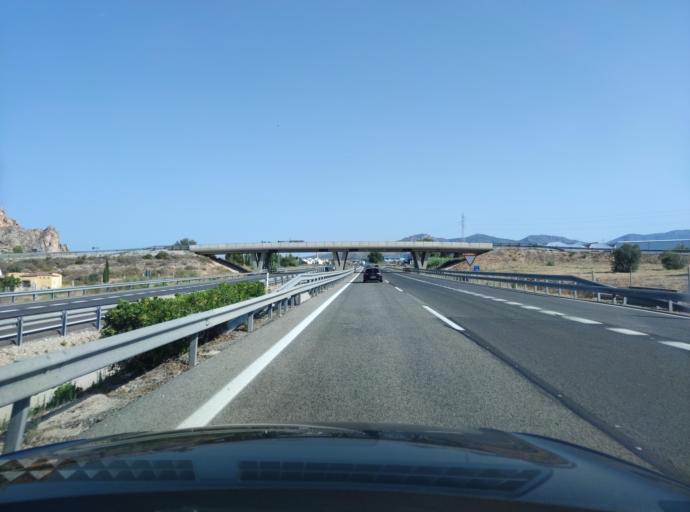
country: ES
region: Valencia
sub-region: Provincia de Alicante
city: Sax
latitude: 38.5366
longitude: -0.8094
